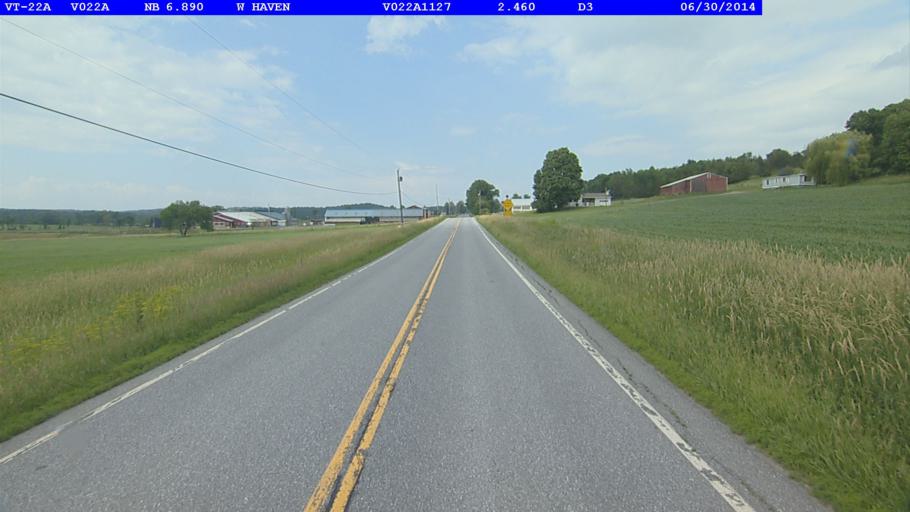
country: US
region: Vermont
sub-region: Rutland County
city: Fair Haven
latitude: 43.6618
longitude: -73.2910
